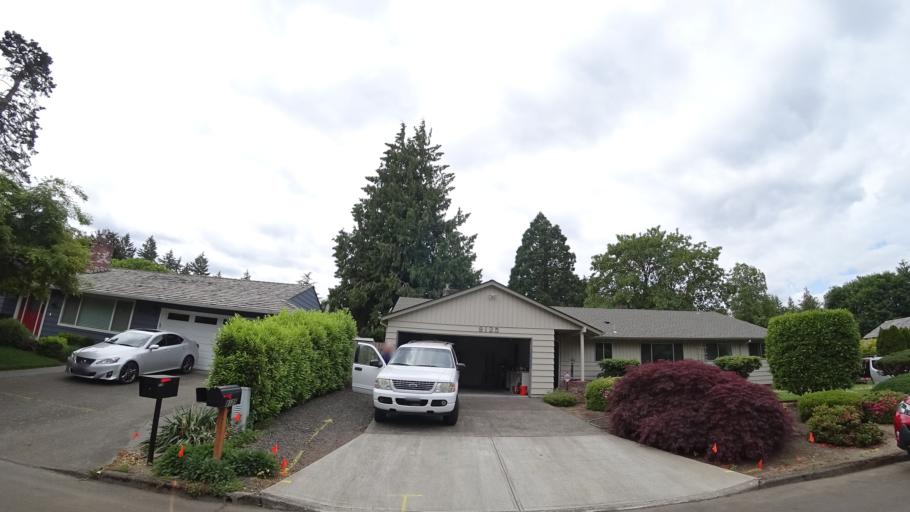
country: US
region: Oregon
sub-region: Washington County
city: Garden Home-Whitford
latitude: 45.4613
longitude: -122.7682
